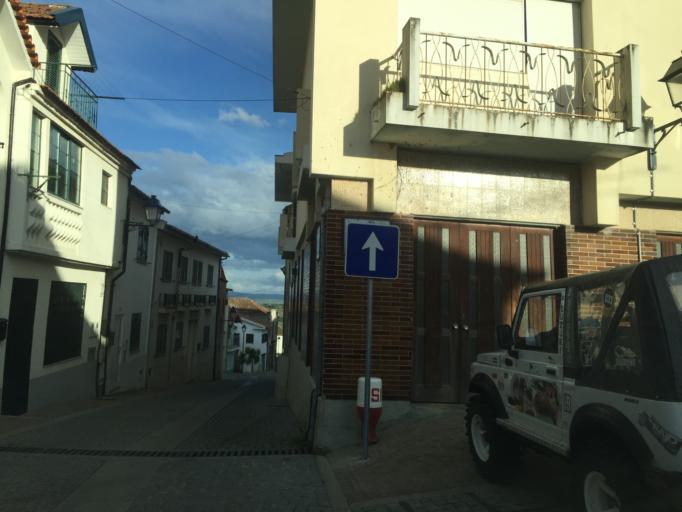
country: PT
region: Braganca
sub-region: Alfandega da Fe
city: Alfandega da Fe
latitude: 41.3426
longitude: -6.9660
